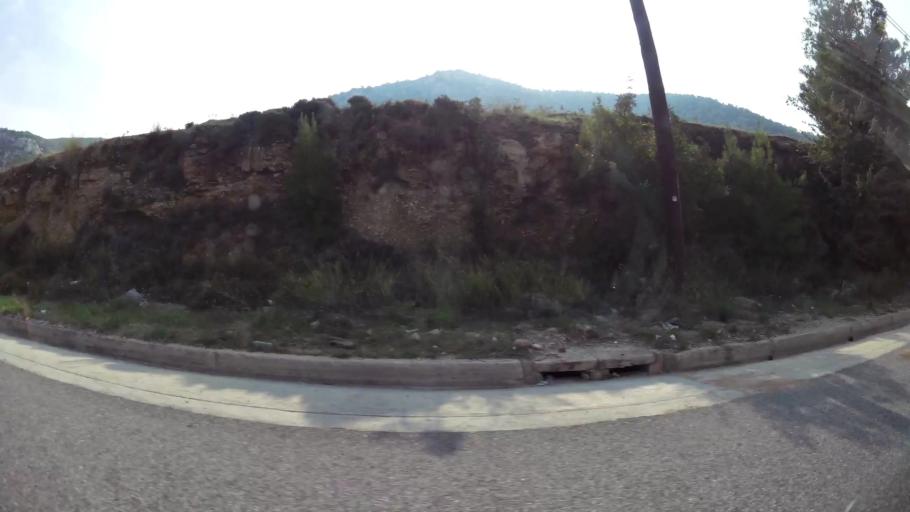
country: GR
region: Attica
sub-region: Nomarchia Athinas
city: Petroupolis
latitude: 38.0457
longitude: 23.6450
